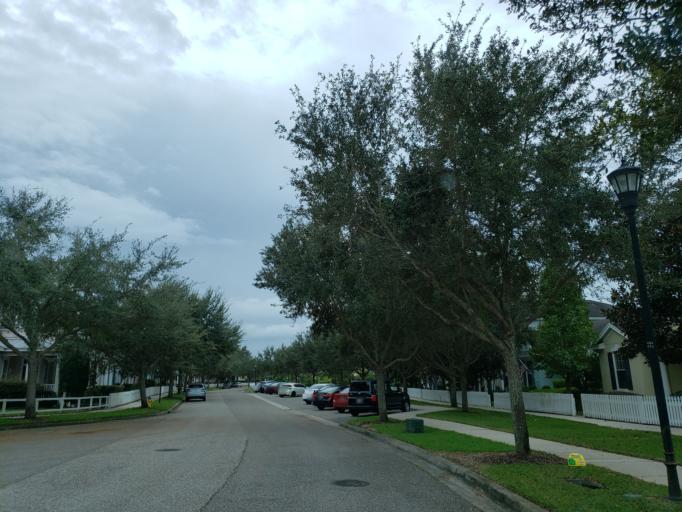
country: US
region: Florida
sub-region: Hillsborough County
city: Riverview
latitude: 27.8913
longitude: -82.3139
